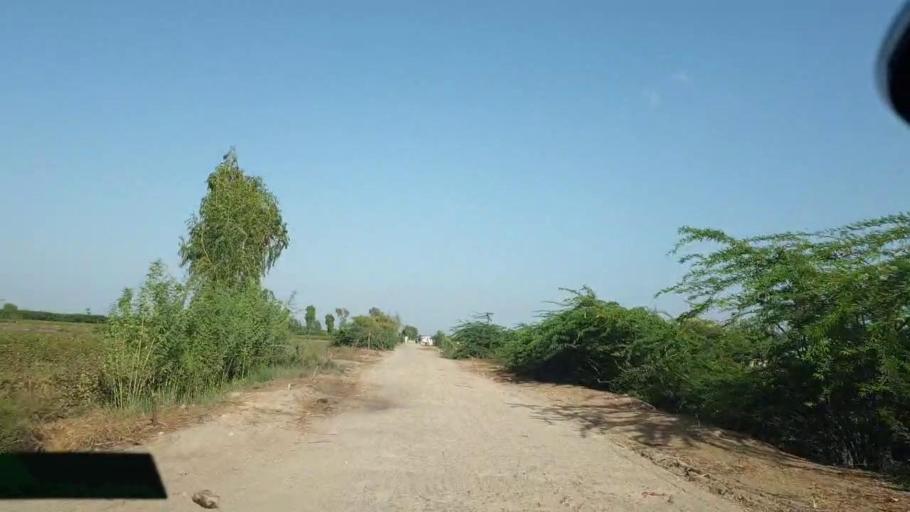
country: PK
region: Sindh
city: Naukot
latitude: 24.7408
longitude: 69.2031
